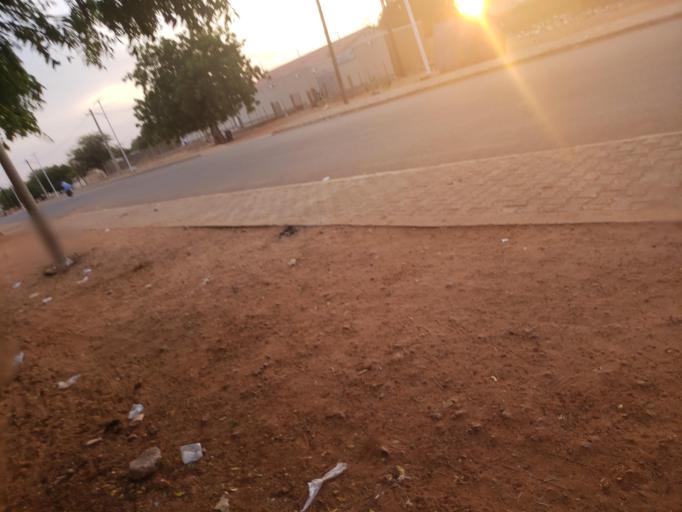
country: SN
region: Louga
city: Ndibene Dahra
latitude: 15.4007
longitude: -15.1128
